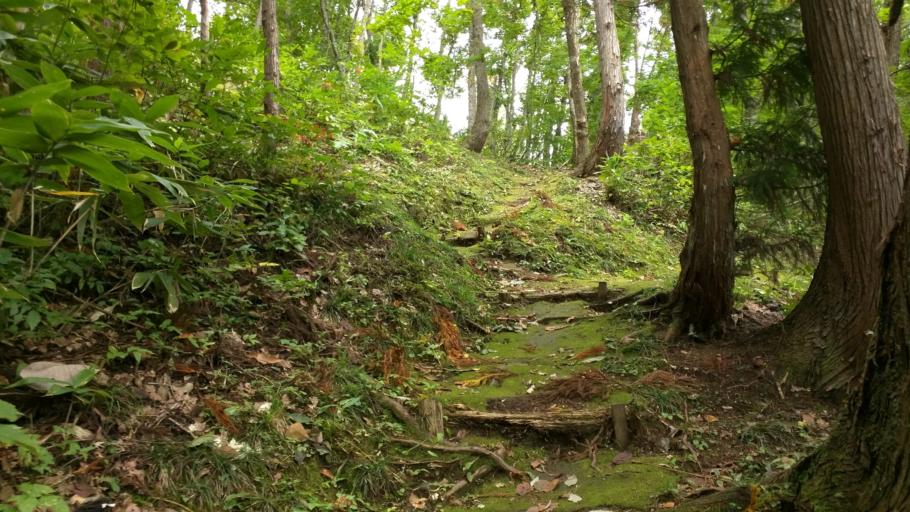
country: JP
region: Fukushima
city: Kitakata
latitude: 37.4584
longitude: 139.7272
